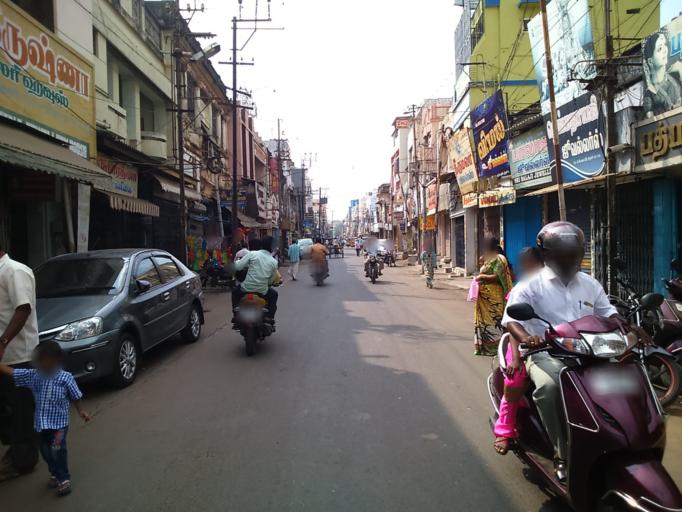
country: IN
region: Tamil Nadu
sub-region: Tiruchchirappalli
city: Tiruchirappalli
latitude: 10.8198
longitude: 78.6969
